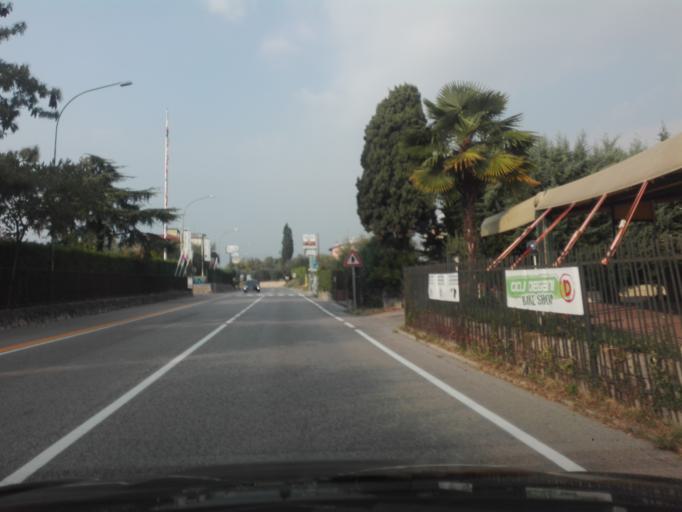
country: IT
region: Veneto
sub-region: Provincia di Verona
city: Lazise
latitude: 45.4966
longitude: 10.7384
